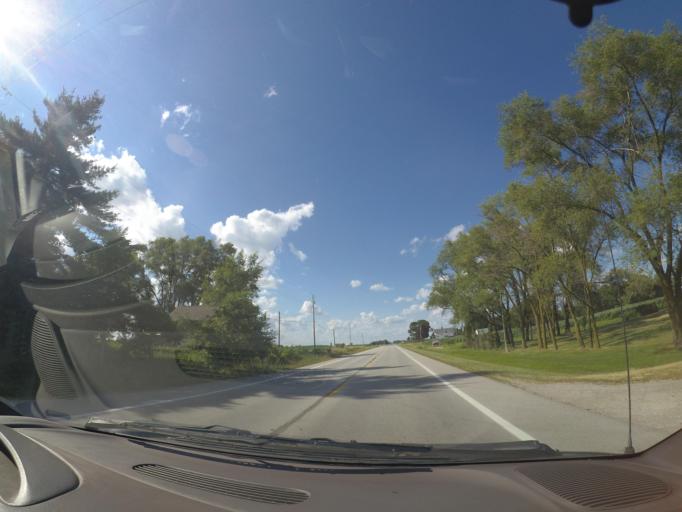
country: US
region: Ohio
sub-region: Wood County
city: Pemberville
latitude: 41.3444
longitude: -83.4172
